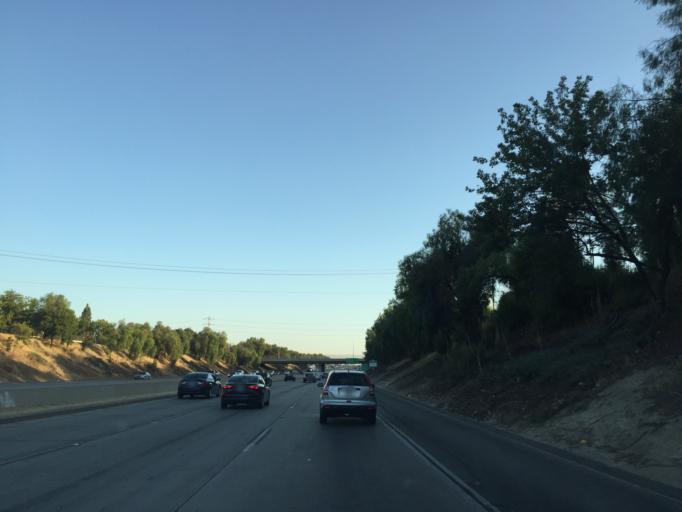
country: US
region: California
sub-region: Fresno County
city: Fresno
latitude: 36.7899
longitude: -119.7846
